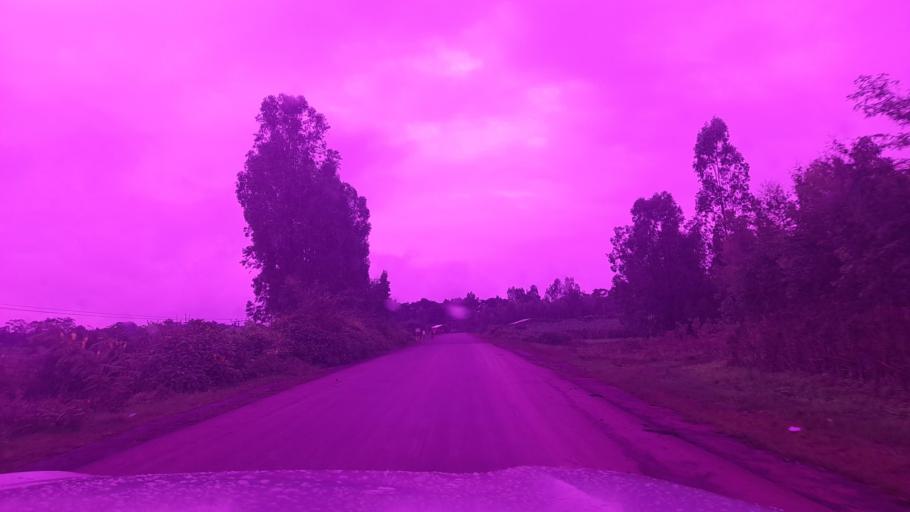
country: ET
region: Oromiya
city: Jima
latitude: 7.7268
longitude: 37.2618
